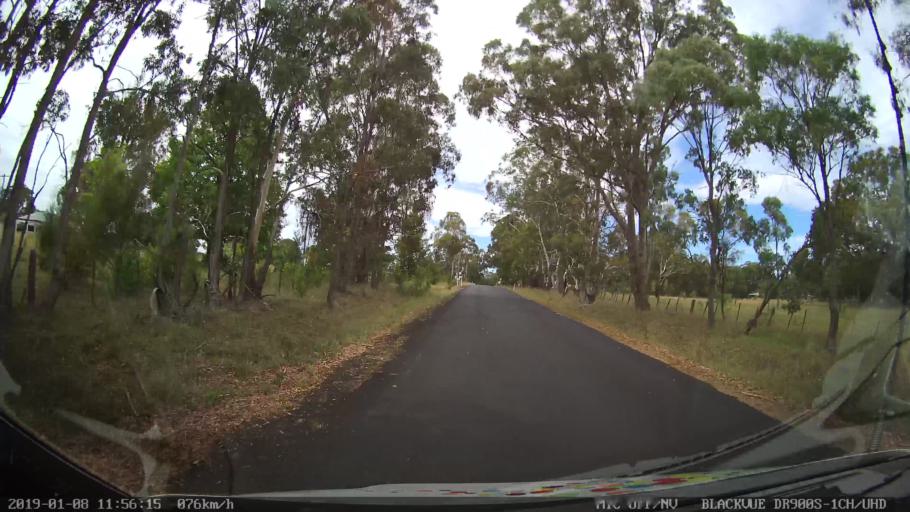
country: AU
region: New South Wales
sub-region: Armidale Dumaresq
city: Armidale
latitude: -30.4380
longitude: 151.5651
